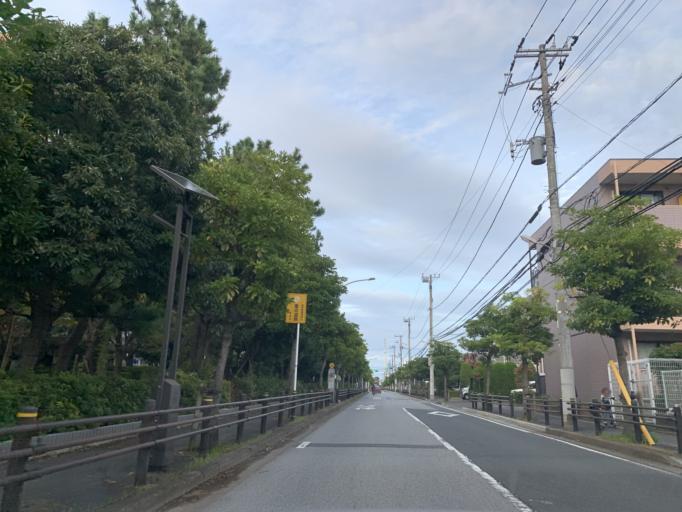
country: JP
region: Tokyo
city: Urayasu
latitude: 35.6503
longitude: 139.9175
